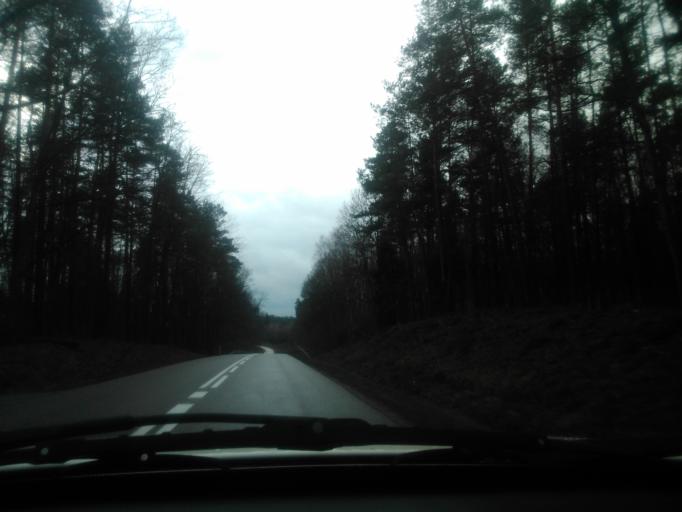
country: PL
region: Kujawsko-Pomorskie
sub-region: Powiat brodnicki
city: Gorzno
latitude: 53.2521
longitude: 19.7152
